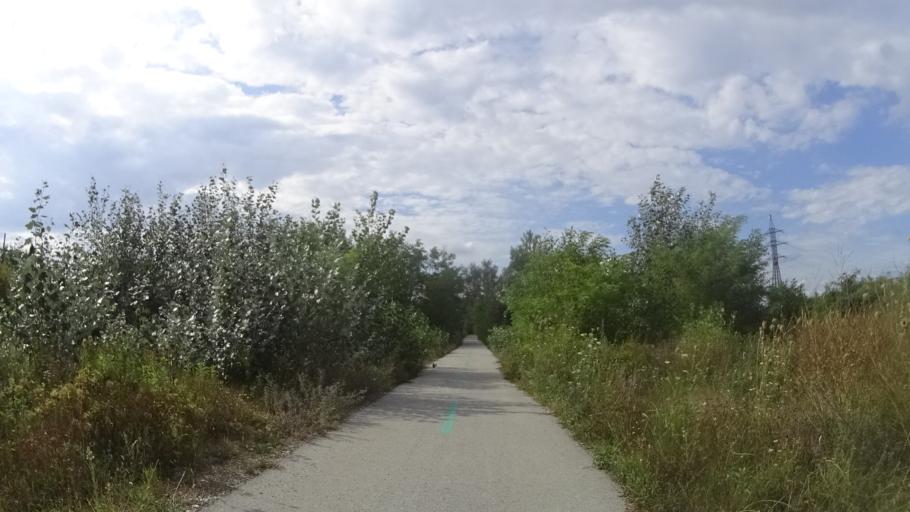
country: SK
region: Trnavsky
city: Gabcikovo
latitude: 47.8843
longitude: 17.5429
